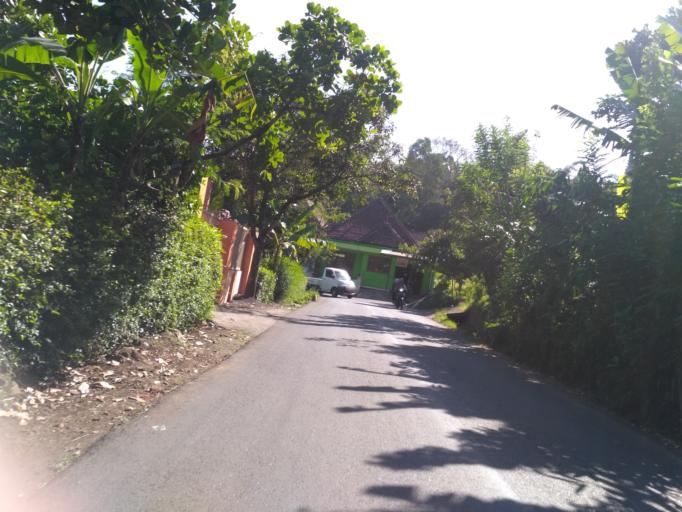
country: ID
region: East Java
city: Singosari
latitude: -7.9273
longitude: 112.6680
